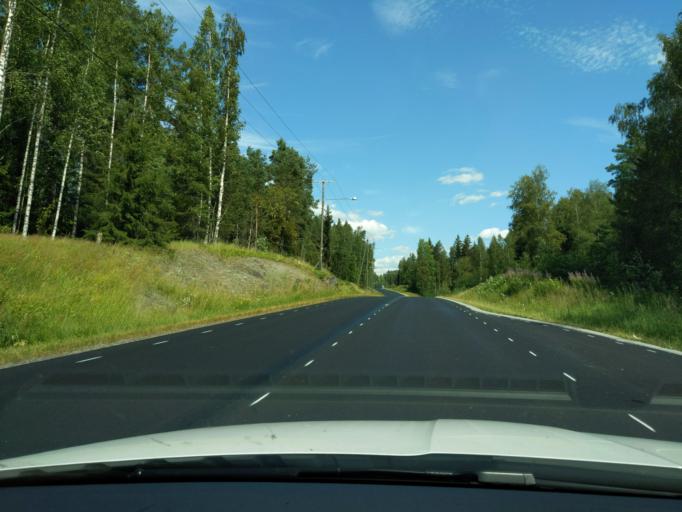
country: FI
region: Paijanne Tavastia
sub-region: Lahti
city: Lahti
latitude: 61.0458
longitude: 25.7677
